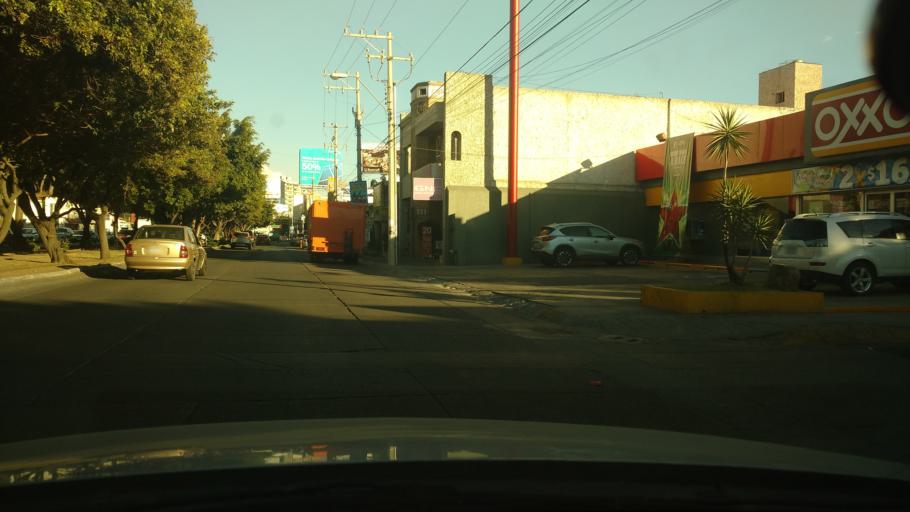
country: MX
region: Guanajuato
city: Leon
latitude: 21.1500
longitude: -101.6929
